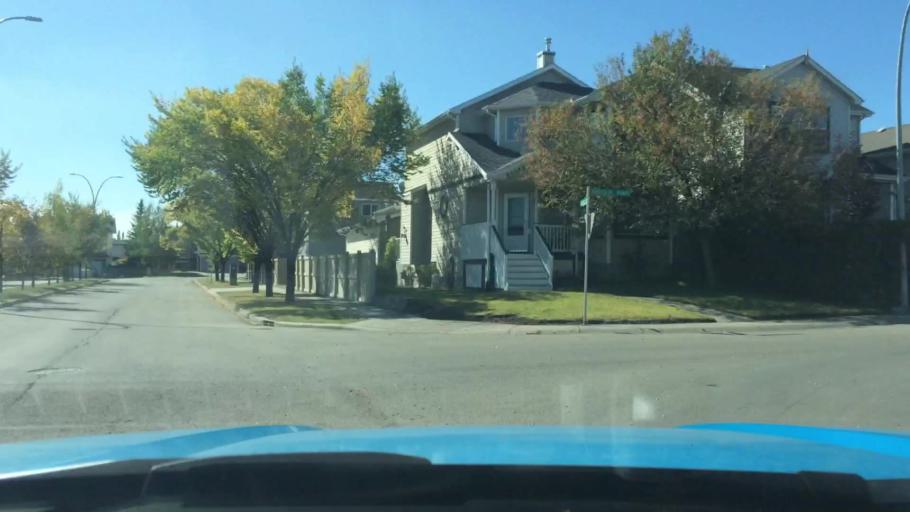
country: CA
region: Alberta
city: Calgary
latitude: 50.9031
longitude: -114.1055
